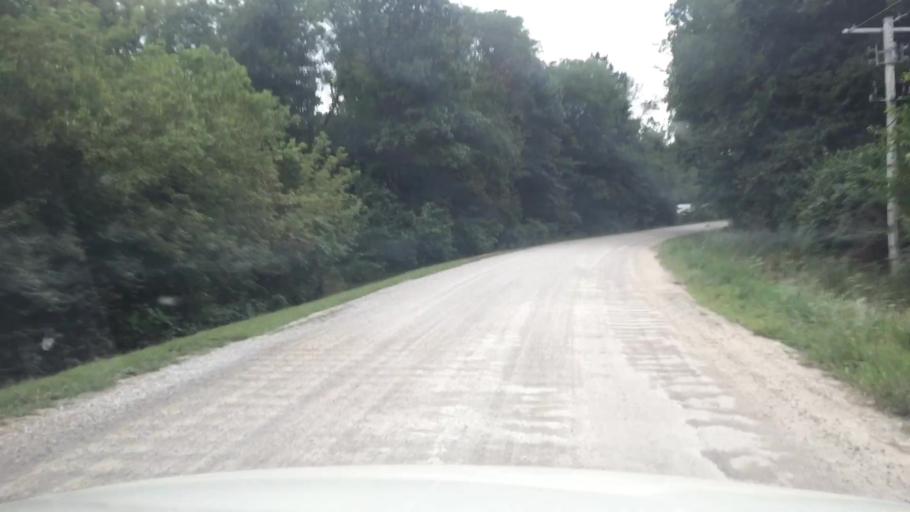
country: US
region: Iowa
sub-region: Story County
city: Huxley
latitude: 41.9095
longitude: -93.5746
